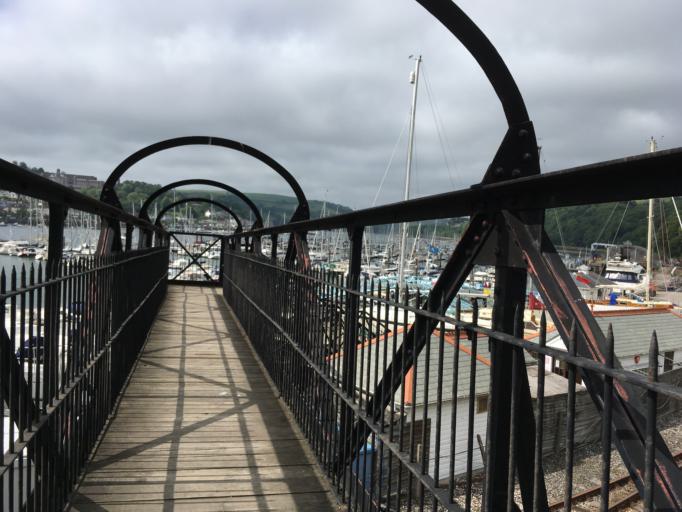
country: GB
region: England
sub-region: Devon
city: Dartmouth
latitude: 50.3498
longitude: -3.5707
